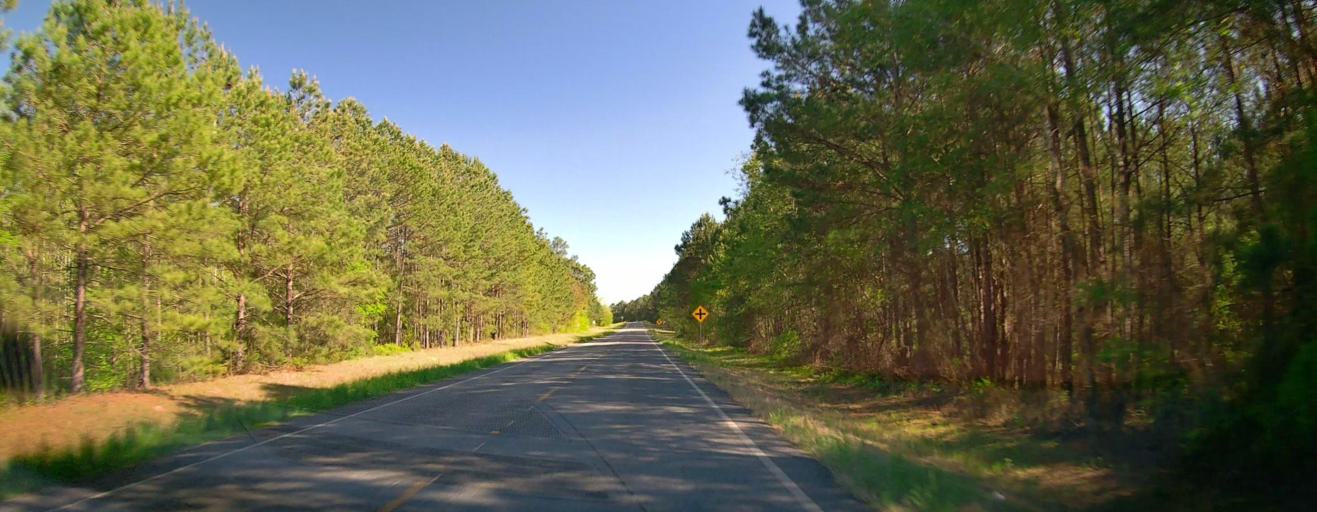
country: US
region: Georgia
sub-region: Wilcox County
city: Rochelle
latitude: 32.0159
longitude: -83.4955
